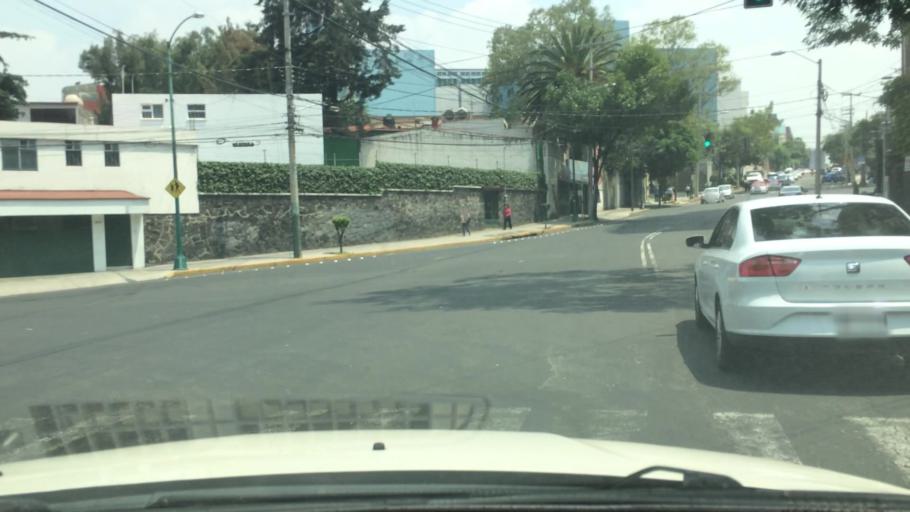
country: MX
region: Mexico City
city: Alvaro Obregon
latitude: 19.3636
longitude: -99.1957
